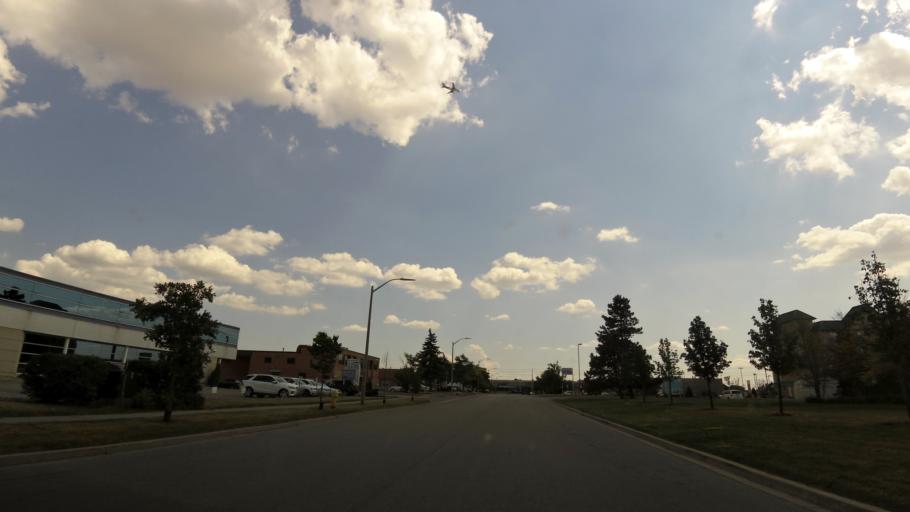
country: CA
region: Ontario
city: Concord
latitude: 43.7762
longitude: -79.5308
